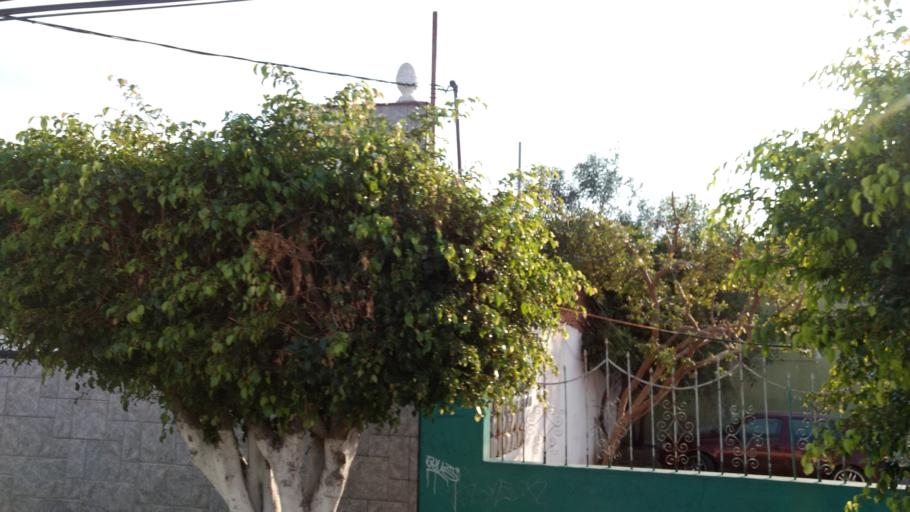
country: MX
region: Guanajuato
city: Leon
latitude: 21.1560
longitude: -101.6731
